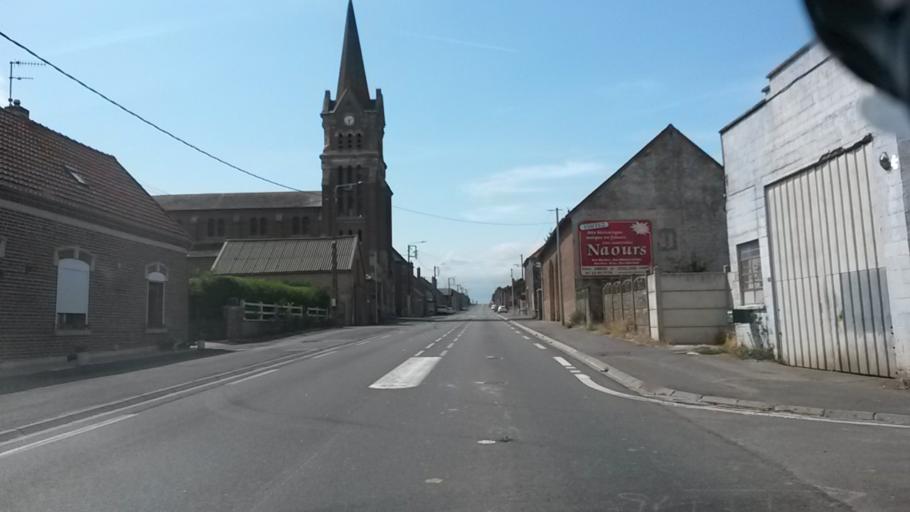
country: FR
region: Nord-Pas-de-Calais
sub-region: Departement du Pas-de-Calais
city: Hermies
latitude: 50.1401
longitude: 3.0323
